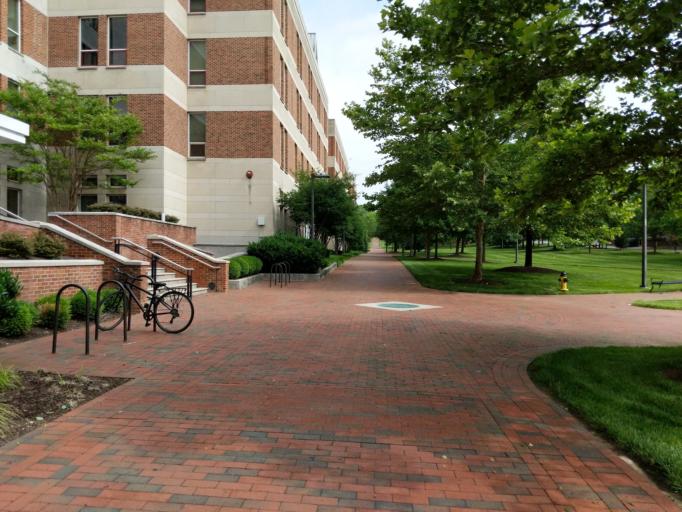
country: US
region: Maryland
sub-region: Prince George's County
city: College Park
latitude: 38.9825
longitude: -76.9468
